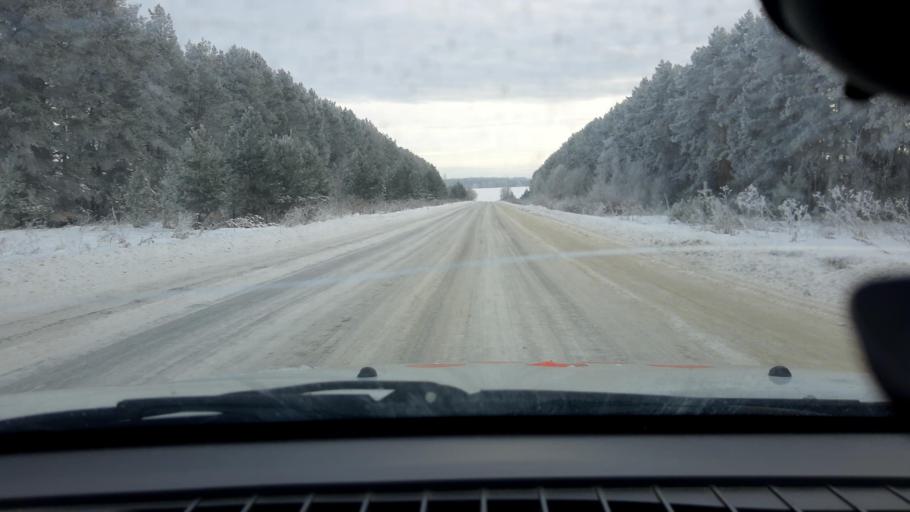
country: RU
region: Nizjnij Novgorod
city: Bogorodsk
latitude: 56.0865
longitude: 43.5643
